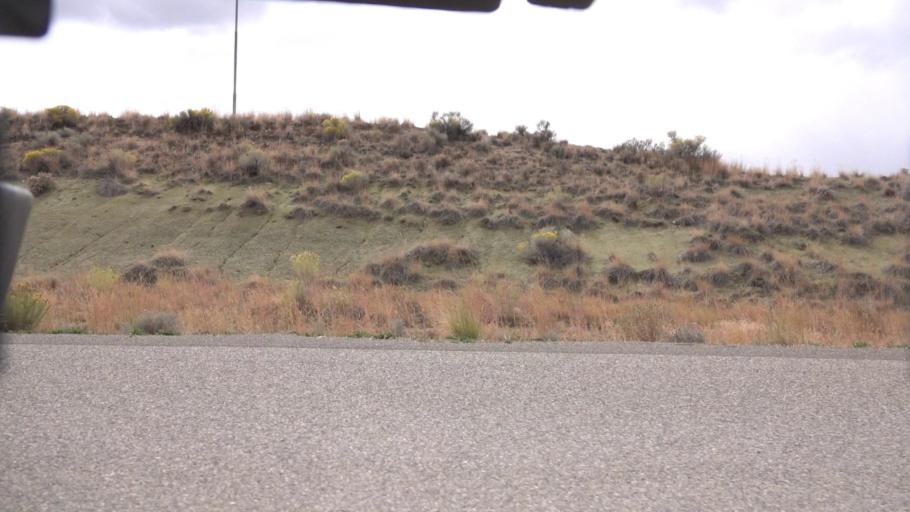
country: US
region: Nevada
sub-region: Elko County
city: Elko
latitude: 40.8475
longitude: -115.7580
